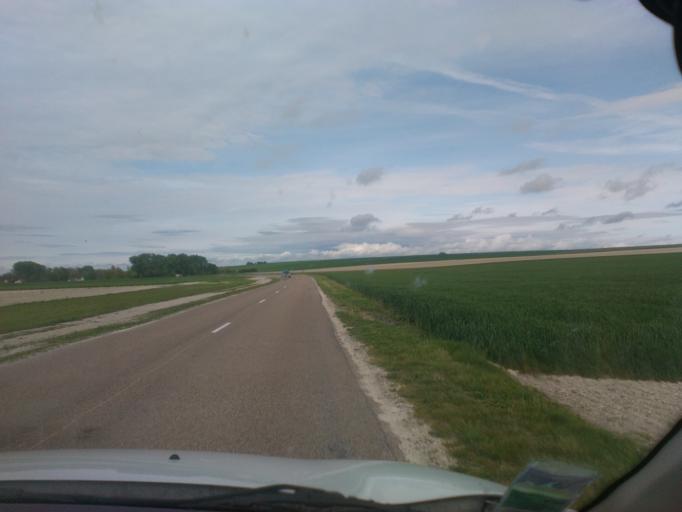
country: FR
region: Champagne-Ardenne
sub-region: Departement de l'Aube
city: Marigny-le-Chatel
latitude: 48.3626
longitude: 3.7224
